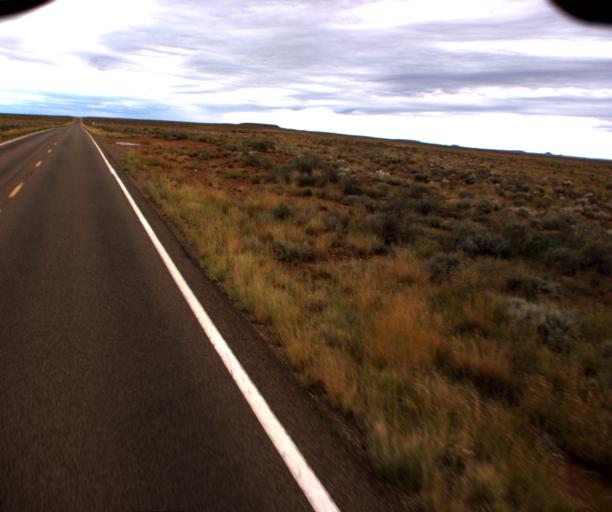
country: US
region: Arizona
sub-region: Navajo County
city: Holbrook
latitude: 34.7616
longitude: -110.1250
